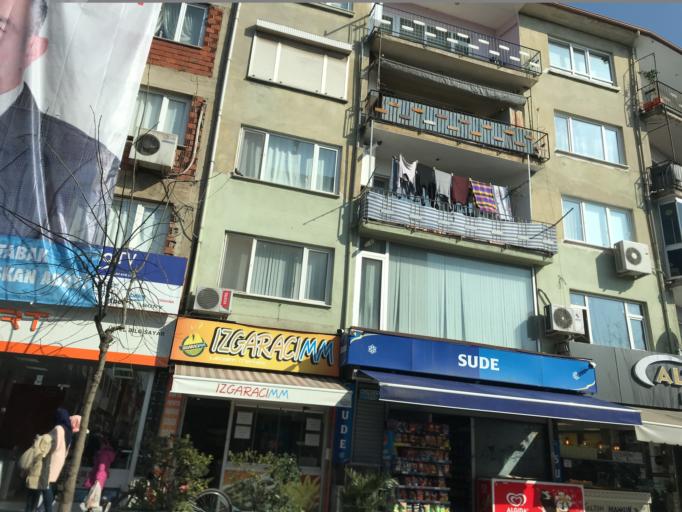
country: TR
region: Yalova
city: Yalova
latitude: 40.6553
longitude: 29.2689
